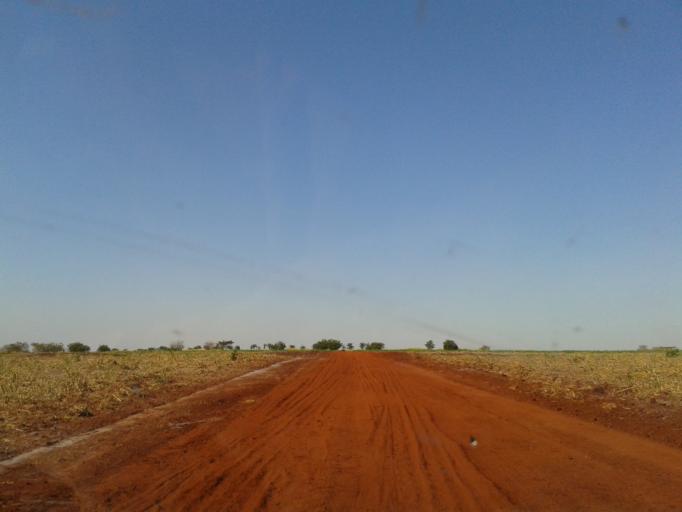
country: BR
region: Minas Gerais
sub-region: Santa Vitoria
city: Santa Vitoria
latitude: -18.7349
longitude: -50.2615
